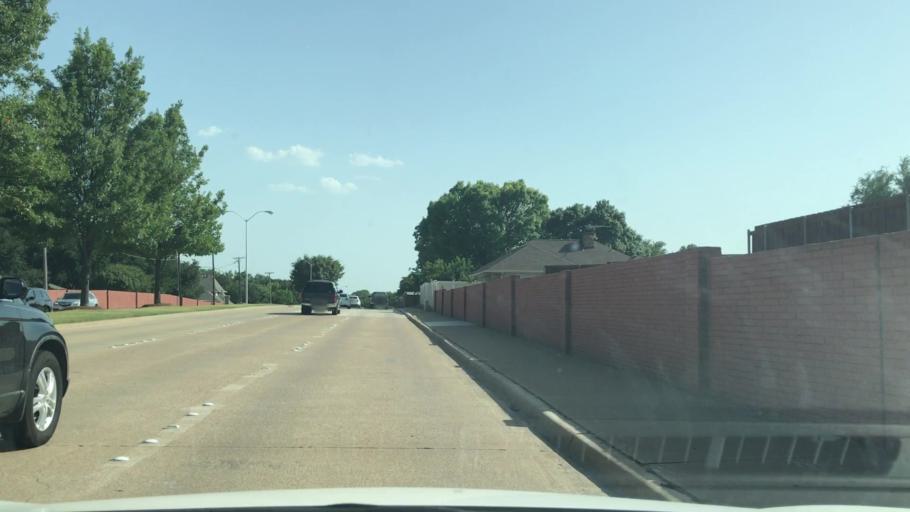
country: US
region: Texas
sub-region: Collin County
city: Plano
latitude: 33.0514
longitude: -96.7516
